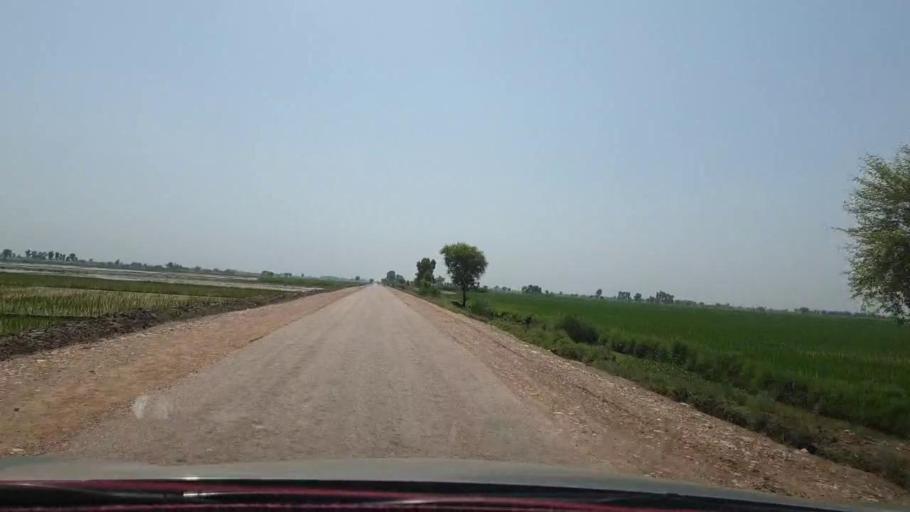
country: PK
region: Sindh
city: Warah
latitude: 27.5656
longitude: 67.8023
